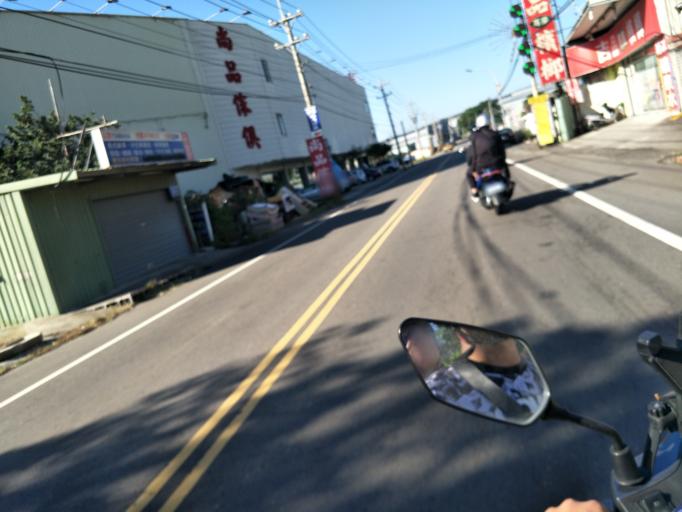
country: TW
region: Taiwan
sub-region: Hsinchu
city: Zhubei
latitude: 24.8327
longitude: 121.0363
